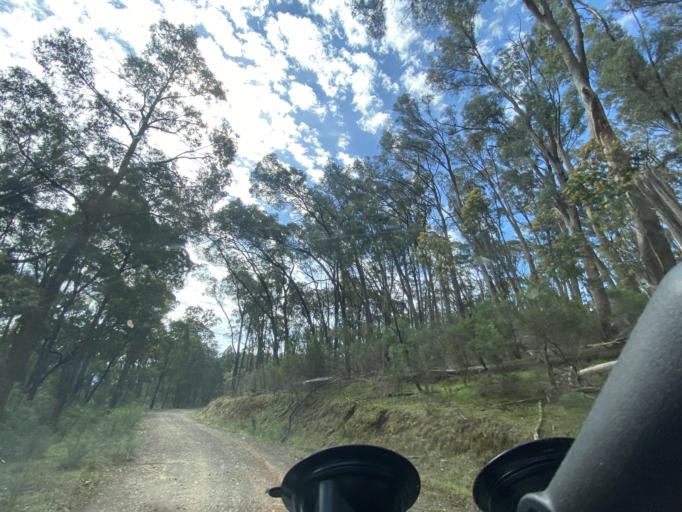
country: AU
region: Victoria
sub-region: Mansfield
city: Mansfield
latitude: -36.8154
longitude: 146.1031
